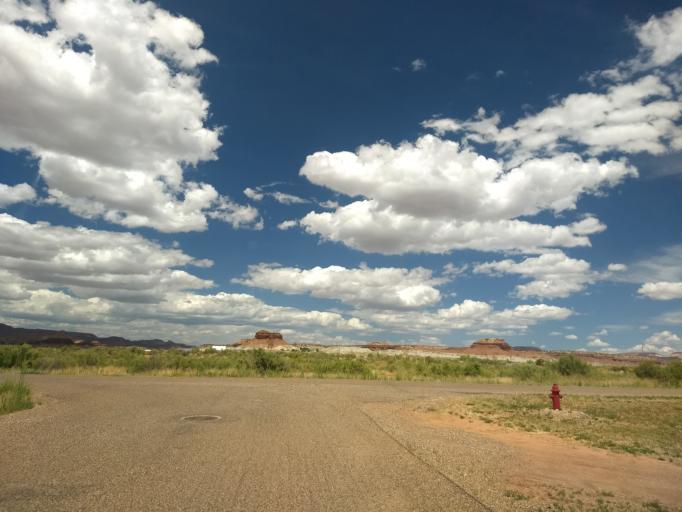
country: US
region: Arizona
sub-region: Coconino County
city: Fredonia
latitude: 36.9612
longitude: -112.5238
